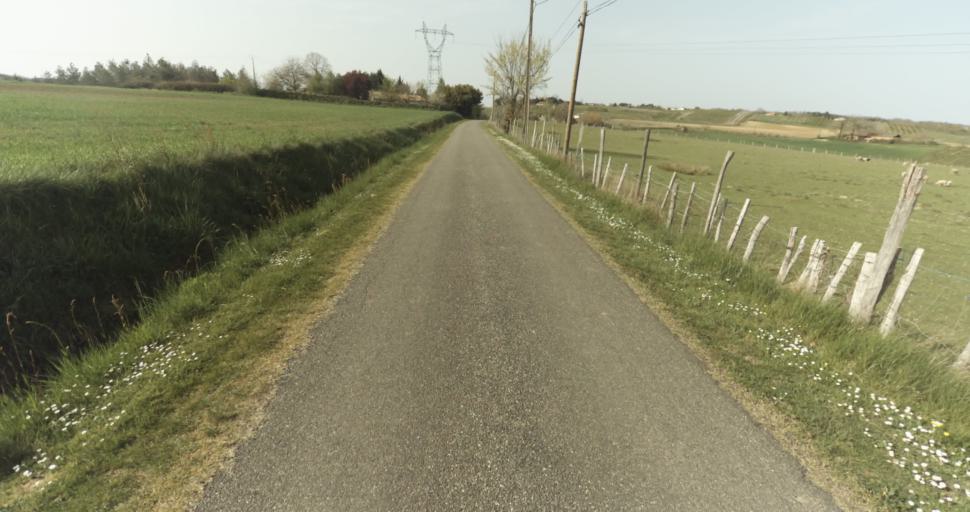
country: FR
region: Midi-Pyrenees
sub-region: Departement du Tarn-et-Garonne
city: Lafrancaise
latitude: 44.1377
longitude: 1.1656
